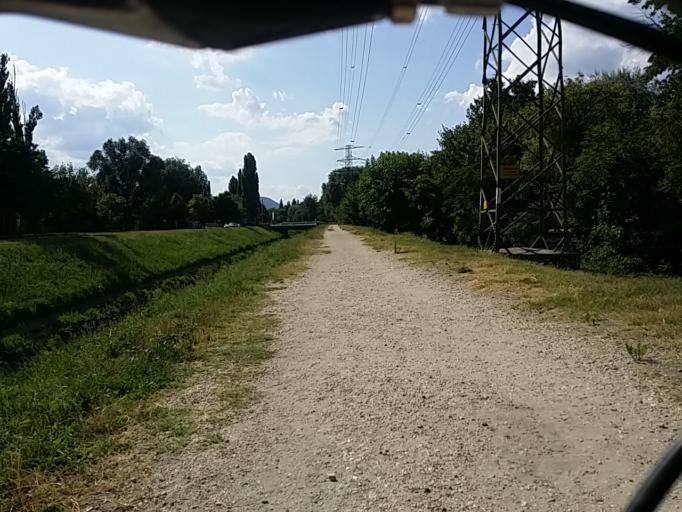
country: HU
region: Budapest
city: Budapest XIII. keruelet
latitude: 47.5407
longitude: 19.0803
